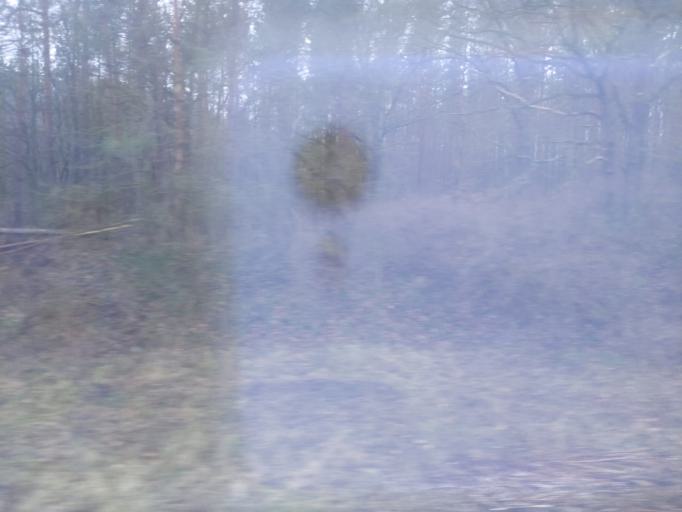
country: DE
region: Saxony
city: Albertstadt
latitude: 51.1065
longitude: 13.7889
